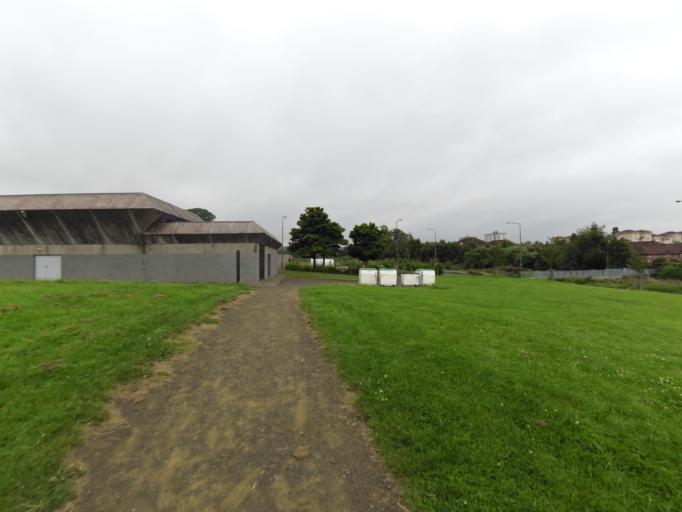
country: GB
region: Scotland
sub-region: West Lothian
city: Seafield
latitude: 55.9325
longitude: -3.1176
